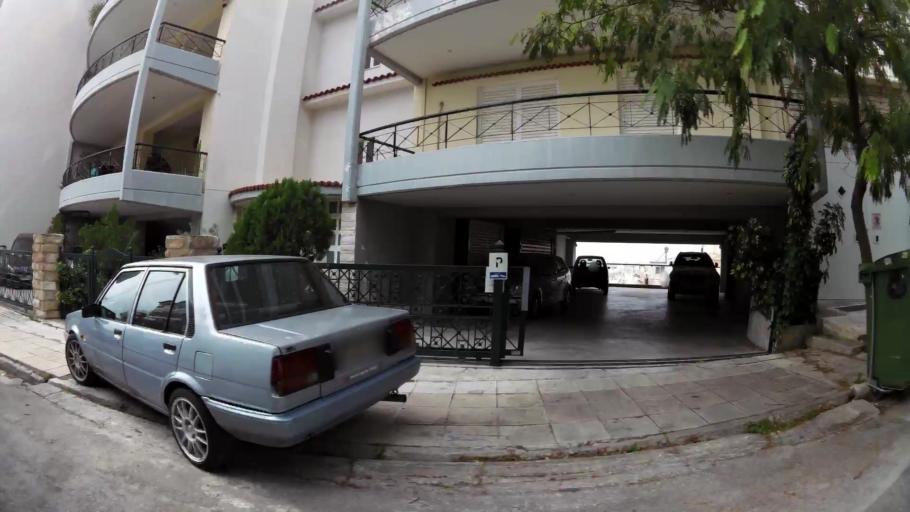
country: GR
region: Attica
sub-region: Nomarchia Athinas
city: Agios Dimitrios
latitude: 37.9295
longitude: 23.7400
